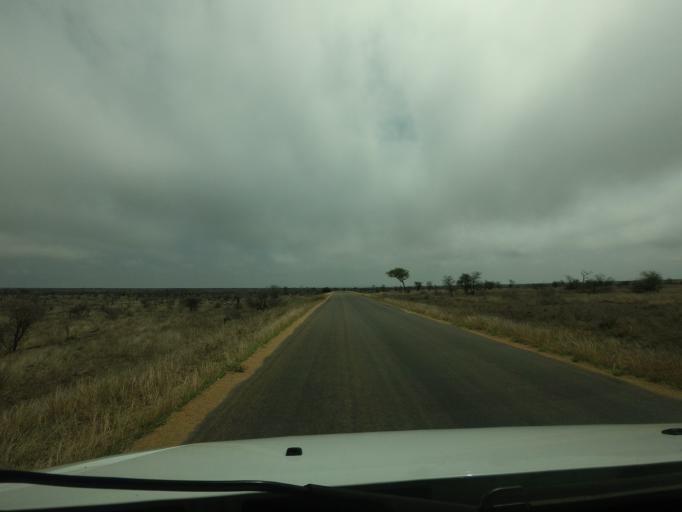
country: ZA
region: Limpopo
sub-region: Mopani District Municipality
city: Phalaborwa
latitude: -24.2027
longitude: 31.7191
